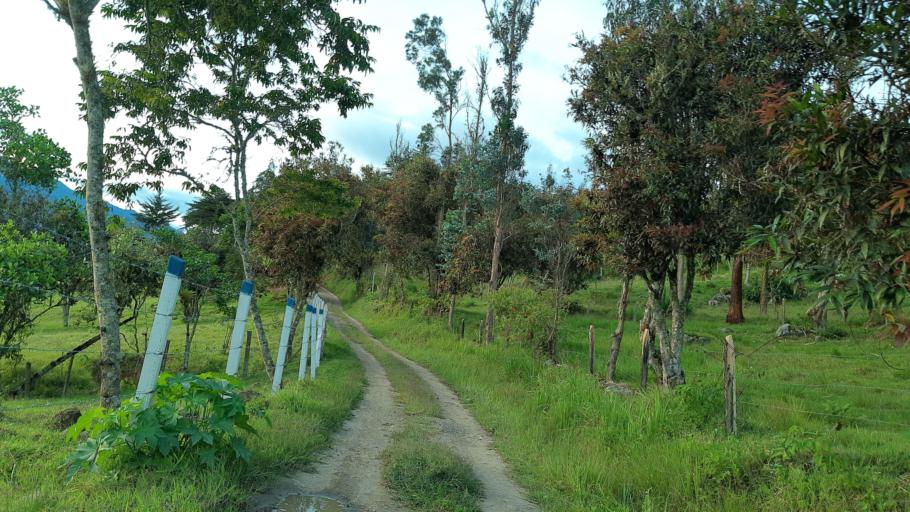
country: CO
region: Boyaca
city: Garagoa
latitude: 5.0560
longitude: -73.3777
